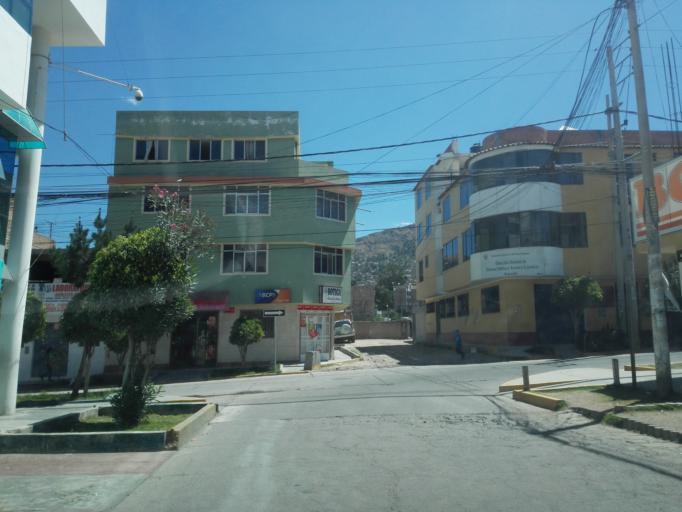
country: PE
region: Ayacucho
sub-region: Provincia de Huamanga
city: Ayacucho
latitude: -13.1509
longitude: -74.2260
